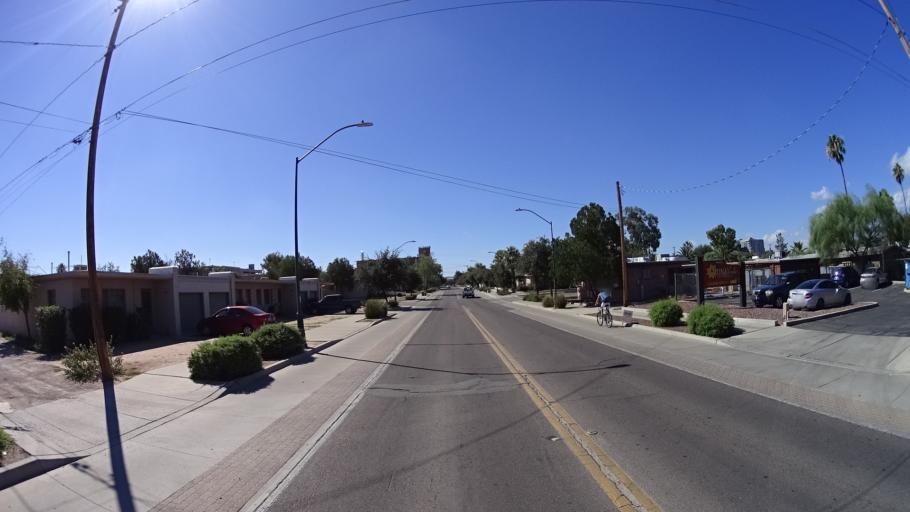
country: US
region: Arizona
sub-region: Pima County
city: Tucson
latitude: 32.2400
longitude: -110.9525
